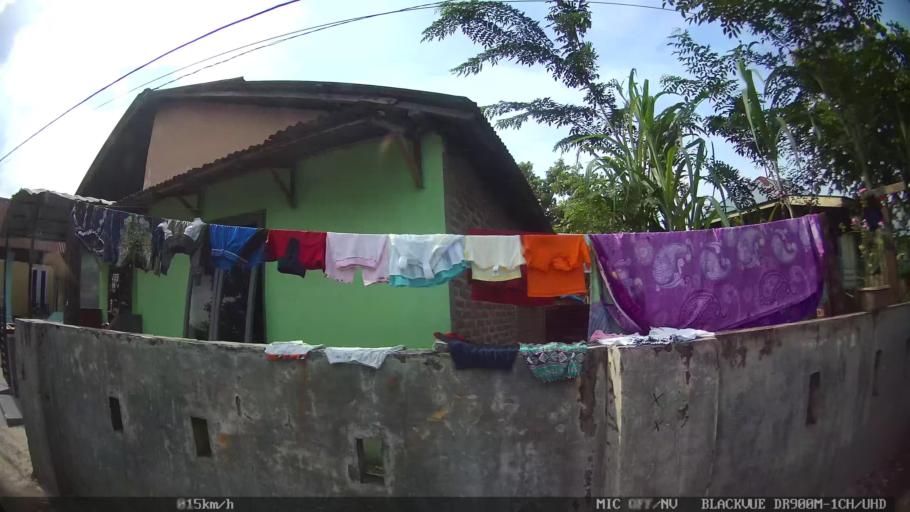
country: ID
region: North Sumatra
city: Binjai
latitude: 3.6041
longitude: 98.4916
